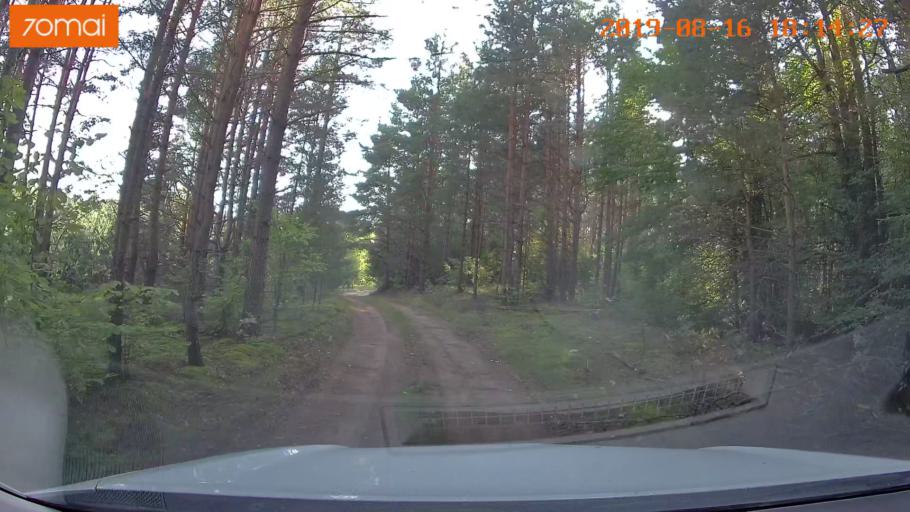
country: BY
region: Mogilev
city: Asipovichy
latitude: 53.2117
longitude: 28.6429
